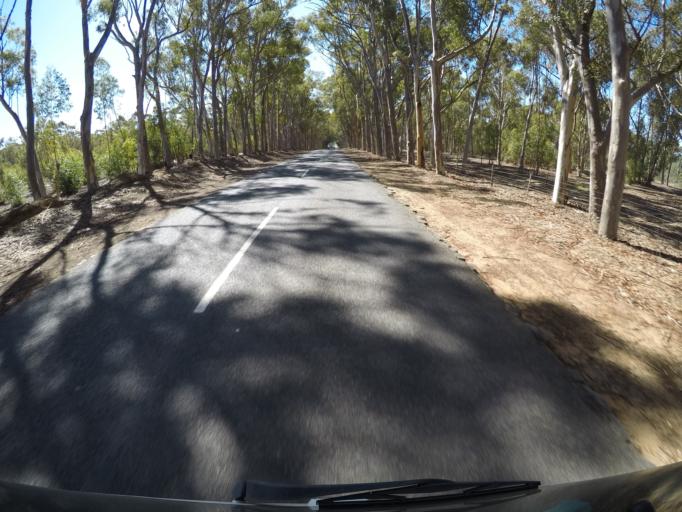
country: ZA
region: Western Cape
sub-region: City of Cape Town
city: Sunset Beach
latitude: -33.7525
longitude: 18.5559
